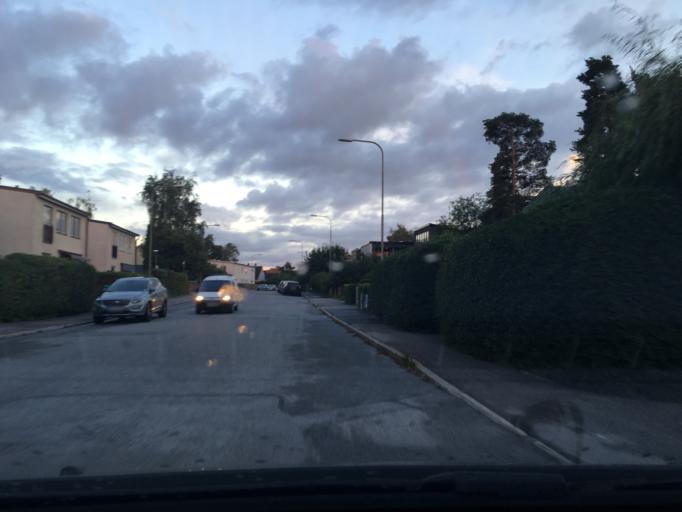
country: SE
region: Stockholm
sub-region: Jarfalla Kommun
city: Jakobsberg
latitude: 59.3765
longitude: 17.8752
